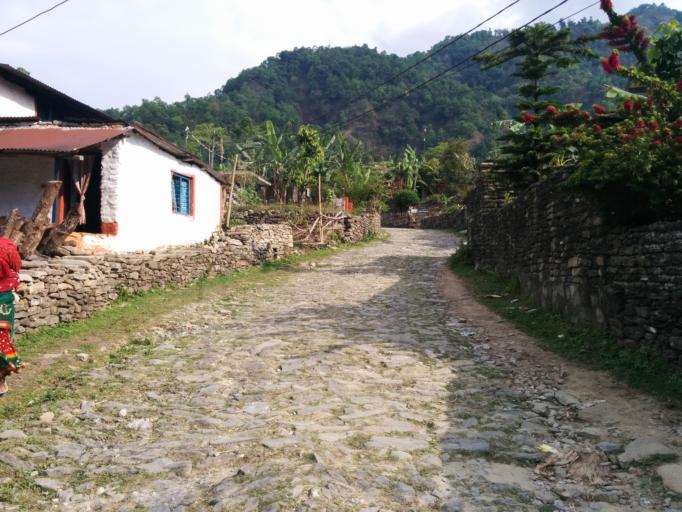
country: NP
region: Western Region
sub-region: Gandaki Zone
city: Pokhara
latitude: 28.2276
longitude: 83.9498
